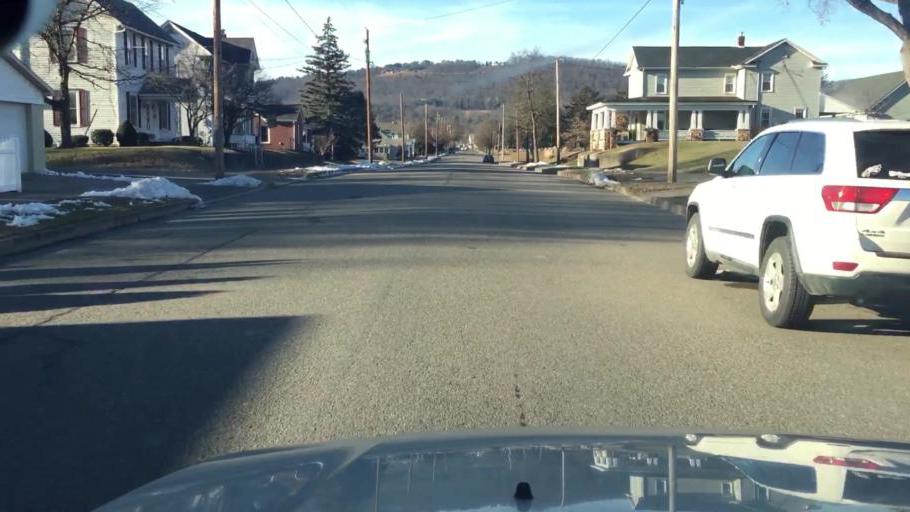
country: US
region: Pennsylvania
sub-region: Columbia County
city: Berwick
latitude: 41.0640
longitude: -76.2342
